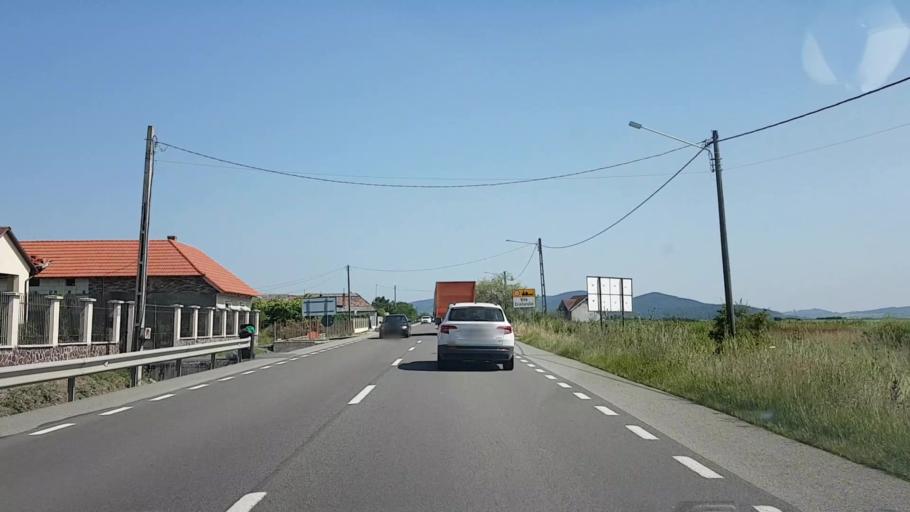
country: RO
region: Bistrita-Nasaud
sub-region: Comuna Sieu-Odorhei
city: Sieu-Odorhei
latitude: 47.1334
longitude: 24.3098
